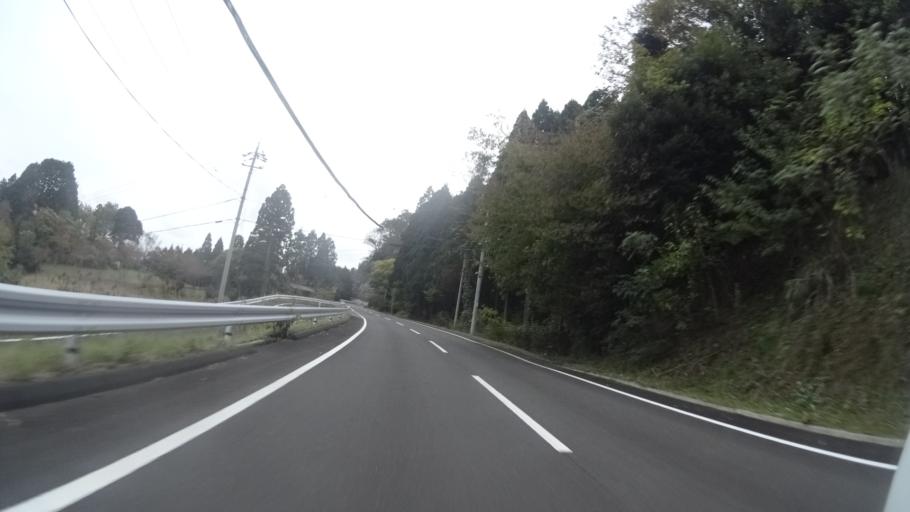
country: JP
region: Kyoto
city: Maizuru
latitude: 35.5661
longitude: 135.4591
